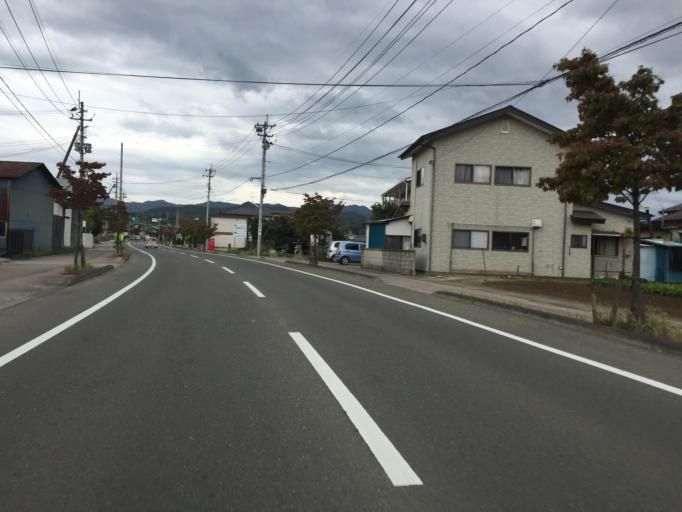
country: JP
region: Fukushima
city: Yanagawamachi-saiwaicho
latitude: 37.8564
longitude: 140.6001
